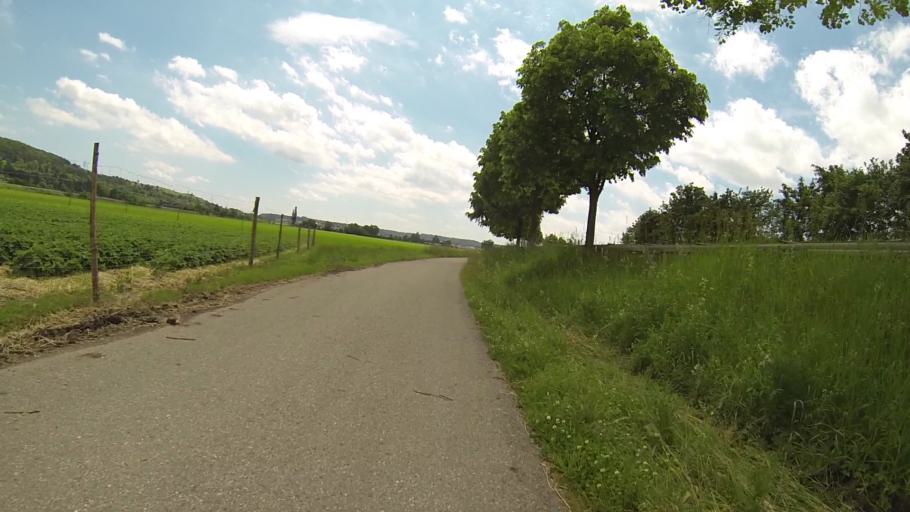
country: DE
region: Baden-Wuerttemberg
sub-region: Regierungsbezirk Stuttgart
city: Bolheim
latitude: 48.6456
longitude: 10.1605
